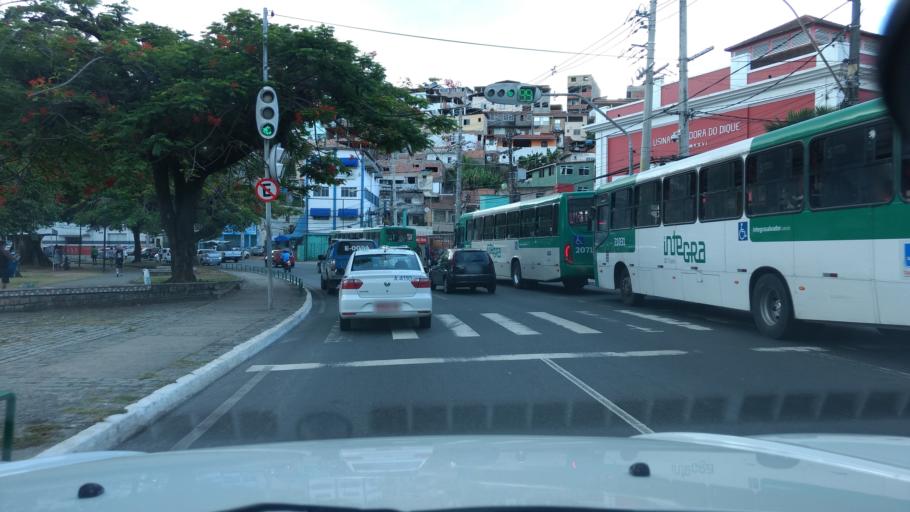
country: BR
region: Bahia
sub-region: Salvador
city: Salvador
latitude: -12.9853
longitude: -38.5053
